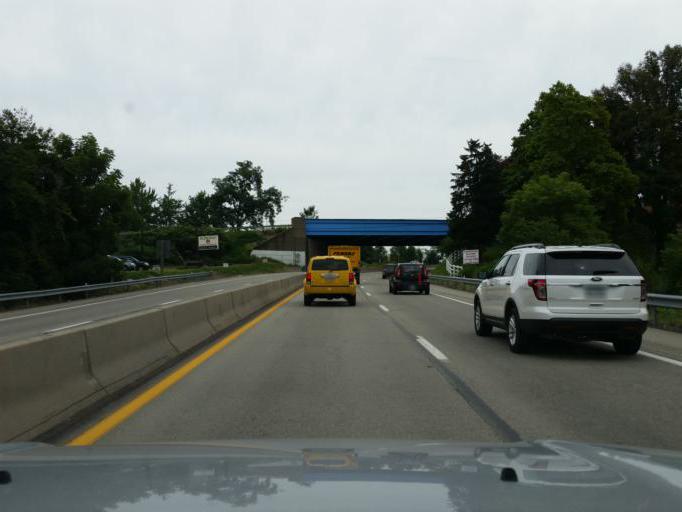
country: US
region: Pennsylvania
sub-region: Westmoreland County
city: Greensburg
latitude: 40.3008
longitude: -79.5201
